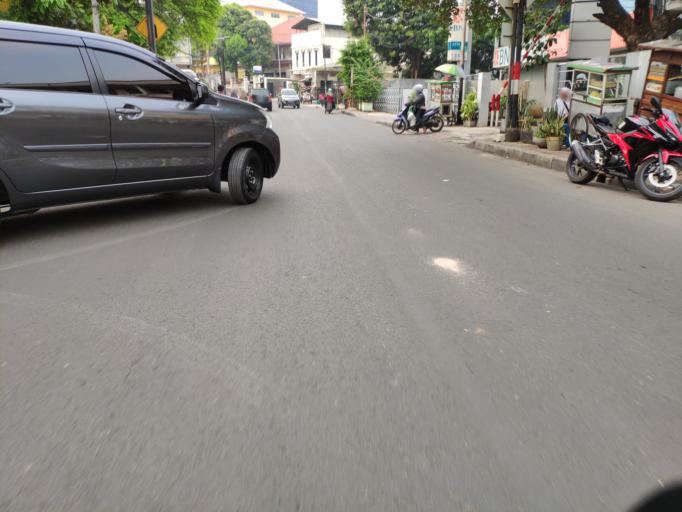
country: ID
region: Jakarta Raya
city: Jakarta
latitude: -6.1942
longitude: 106.8684
